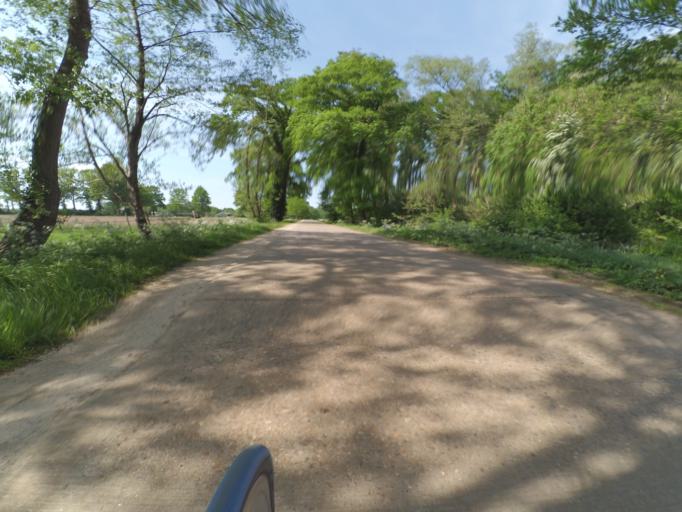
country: NL
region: Overijssel
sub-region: Gemeente Tubbergen
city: Tubbergen
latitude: 52.3566
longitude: 6.7995
